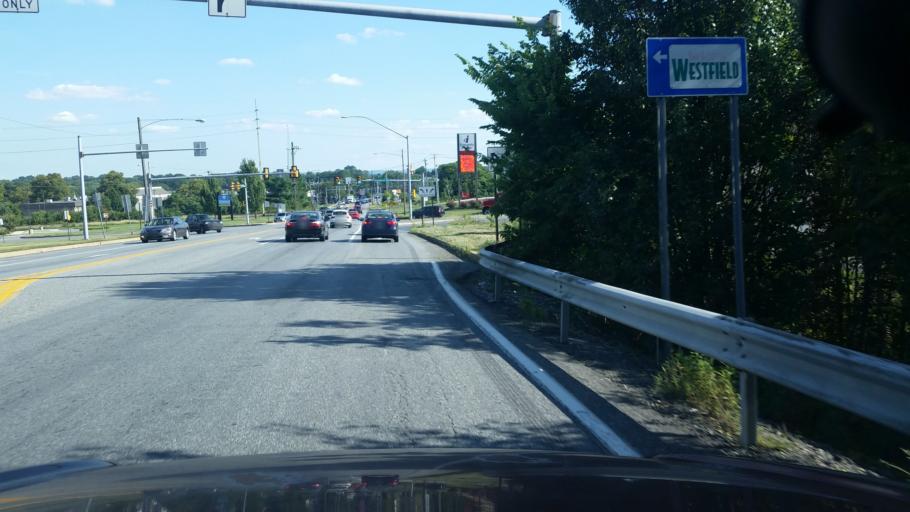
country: US
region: Pennsylvania
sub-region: Lancaster County
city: Mountville
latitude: 40.0511
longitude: -76.3955
